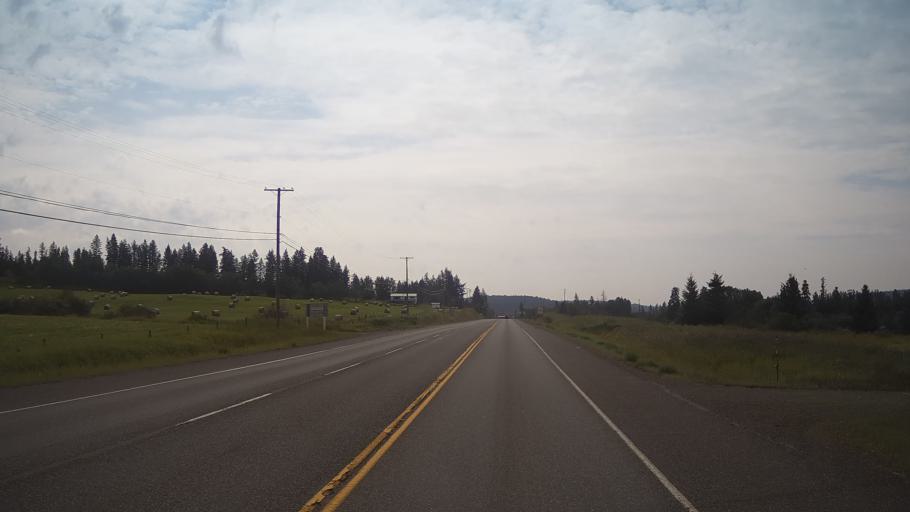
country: CA
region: British Columbia
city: Williams Lake
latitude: 51.8200
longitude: -121.4899
